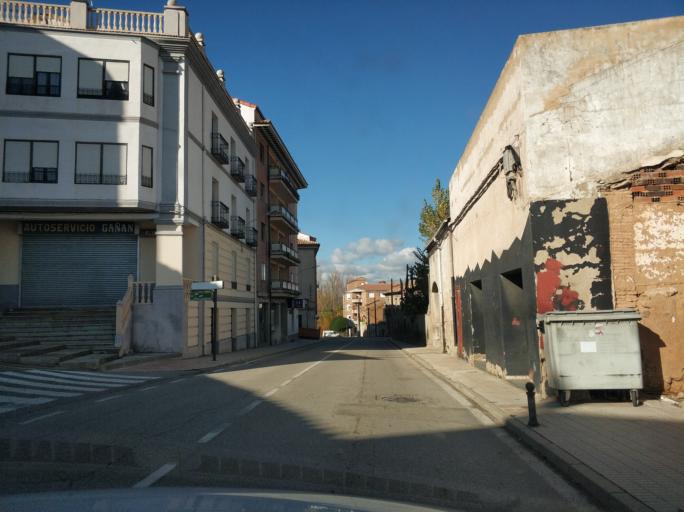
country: ES
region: Castille and Leon
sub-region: Provincia de Soria
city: Almazan
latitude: 41.4871
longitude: -2.5317
